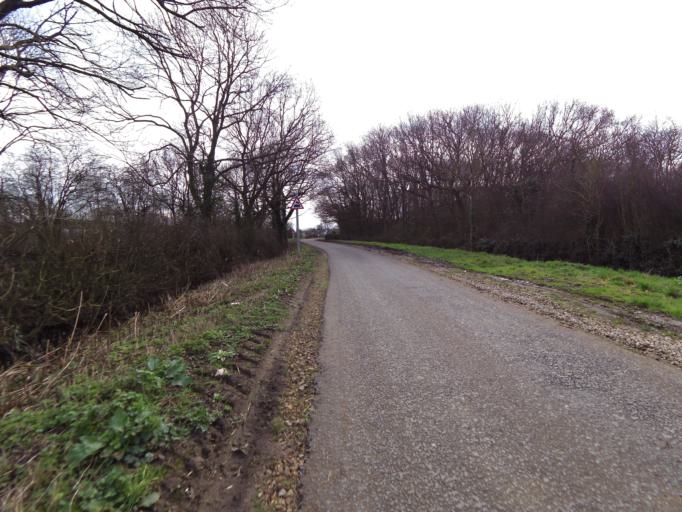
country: GB
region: England
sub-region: Doncaster
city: Moss
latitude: 53.5886
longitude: -1.1259
